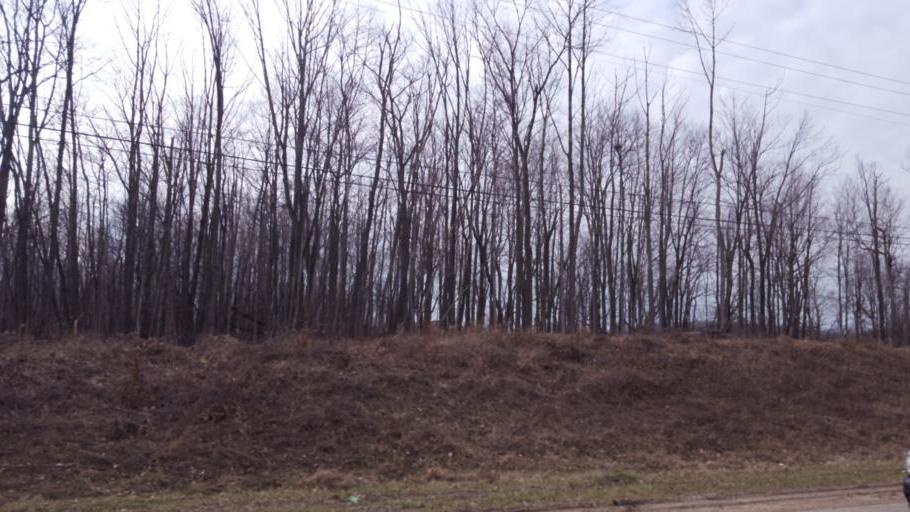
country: US
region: Ohio
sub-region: Richland County
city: Mansfield
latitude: 40.7354
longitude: -82.5517
